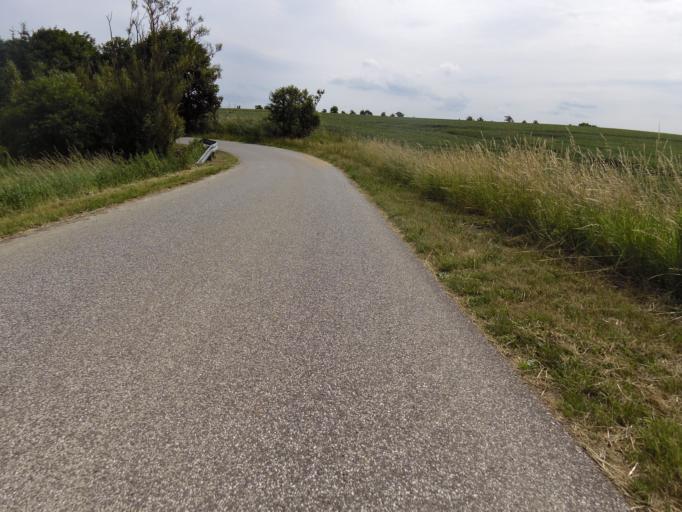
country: DK
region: Central Jutland
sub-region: Holstebro Kommune
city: Holstebro
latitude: 56.4274
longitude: 8.6494
